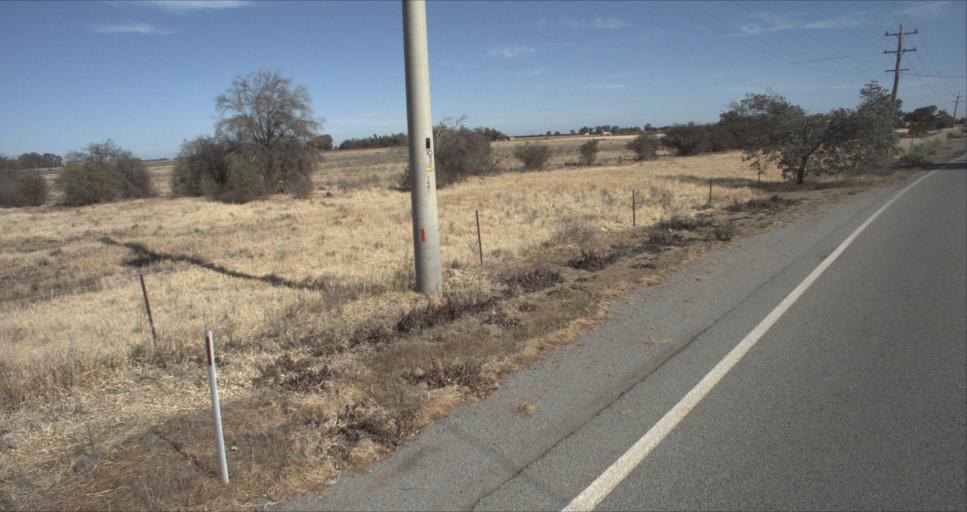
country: AU
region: New South Wales
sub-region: Leeton
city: Leeton
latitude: -34.6016
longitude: 146.4063
